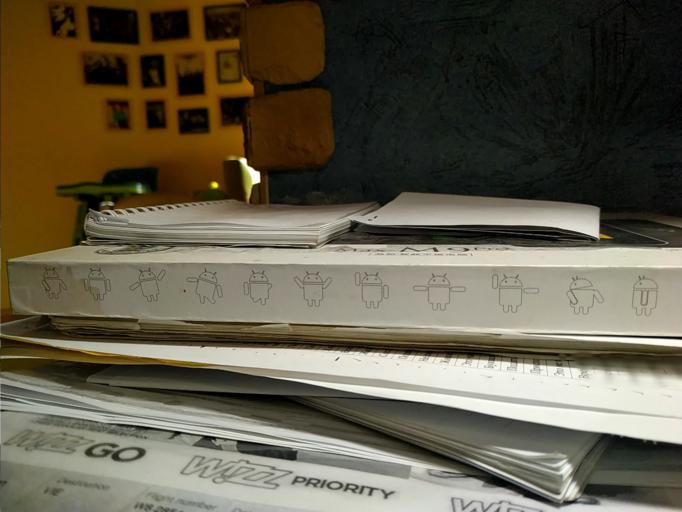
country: RU
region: Novgorod
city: Poddor'ye
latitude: 57.3527
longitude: 31.1510
